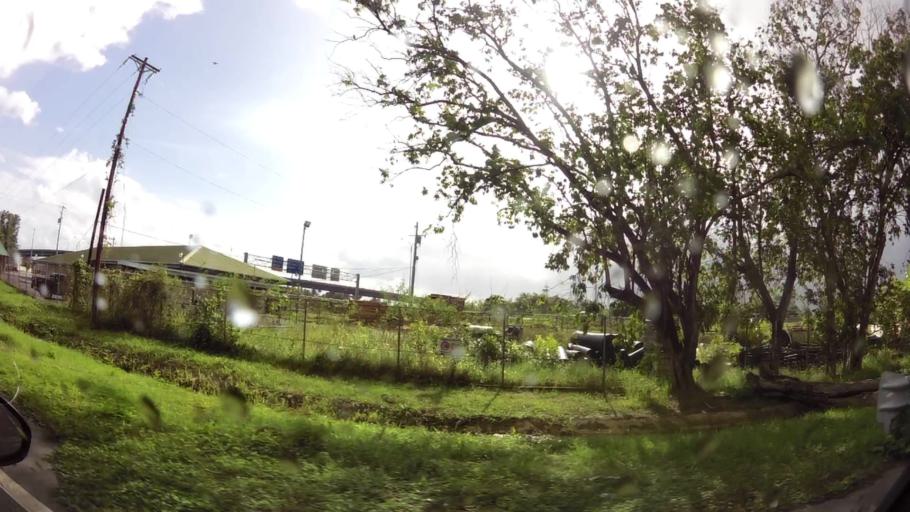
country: TT
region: Tunapuna/Piarco
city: Tunapuna
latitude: 10.6349
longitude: -61.4299
